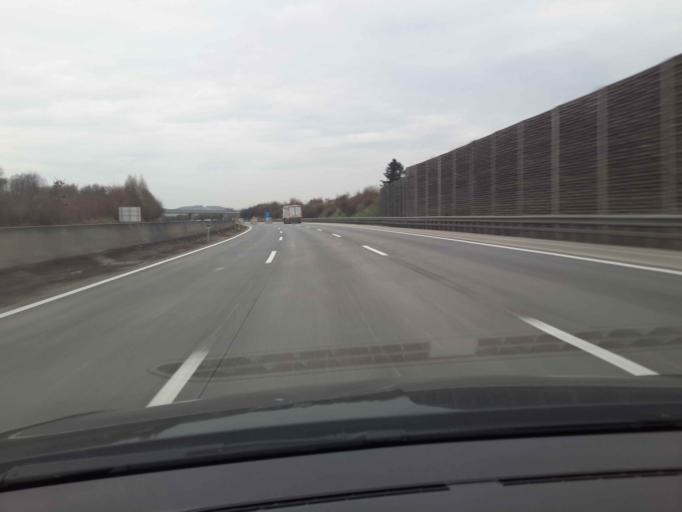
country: AT
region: Lower Austria
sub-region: Politischer Bezirk Melk
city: Melk
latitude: 48.2178
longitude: 15.3259
